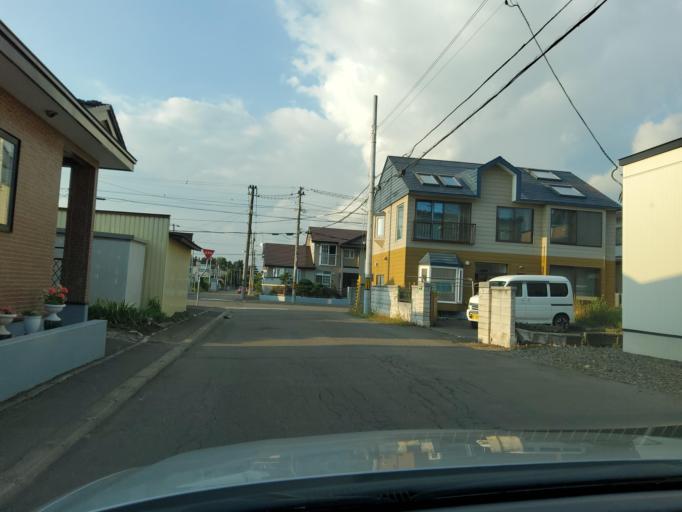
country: JP
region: Hokkaido
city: Obihiro
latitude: 42.9207
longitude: 143.1555
